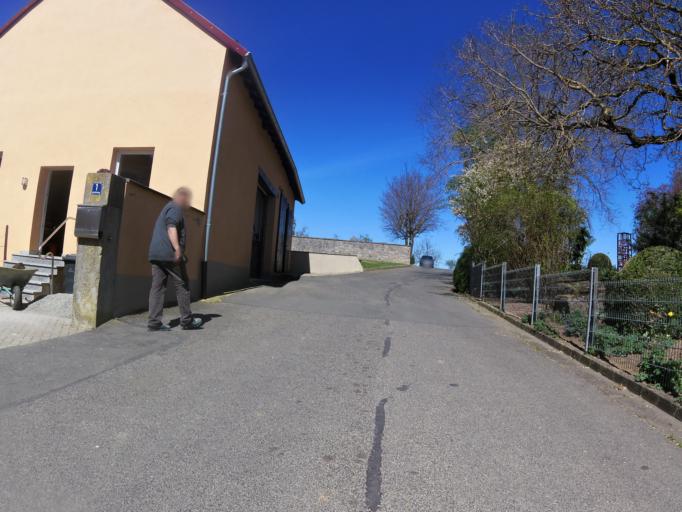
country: DE
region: Bavaria
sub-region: Regierungsbezirk Unterfranken
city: Biebelried
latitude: 49.7974
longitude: 10.0828
